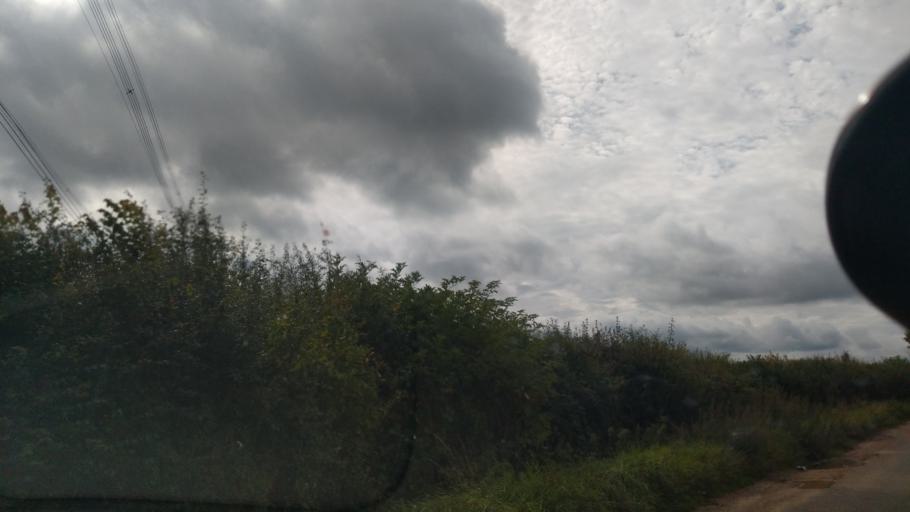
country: GB
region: England
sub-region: Wiltshire
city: Chippenham
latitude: 51.4398
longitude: -2.1511
